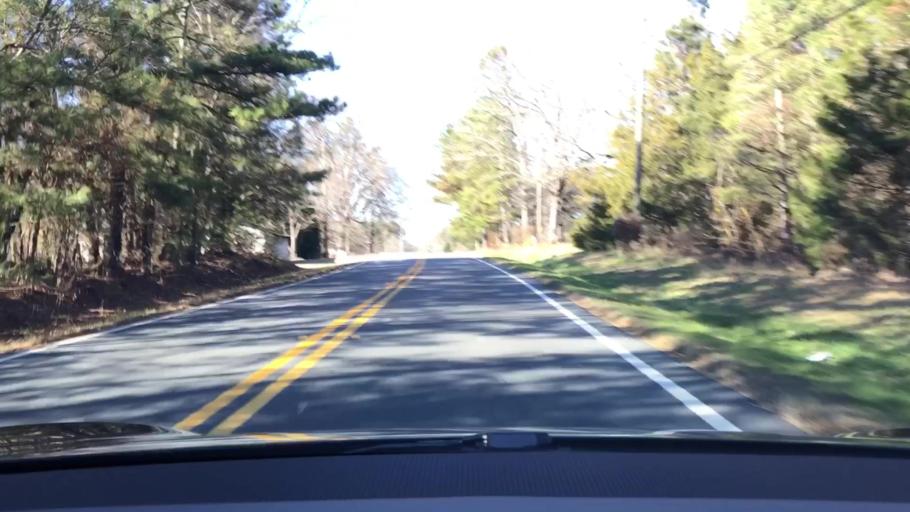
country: US
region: Georgia
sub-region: Barrow County
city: Auburn
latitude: 33.9913
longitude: -83.8008
